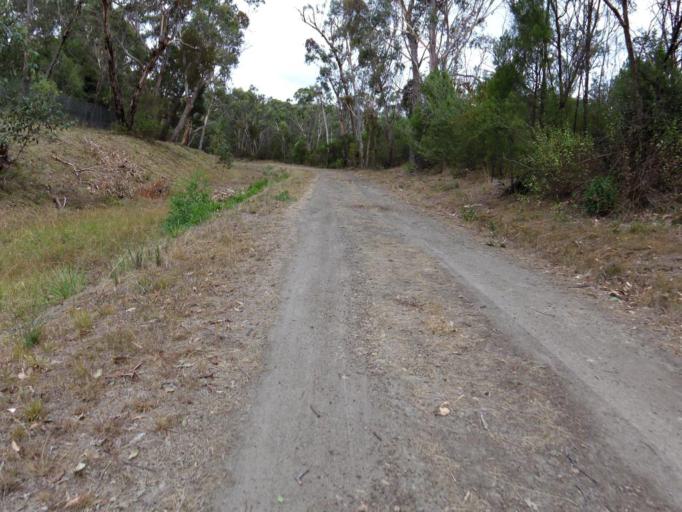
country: AU
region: Victoria
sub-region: Frankston
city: Frankston South
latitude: -38.1821
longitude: 145.1312
